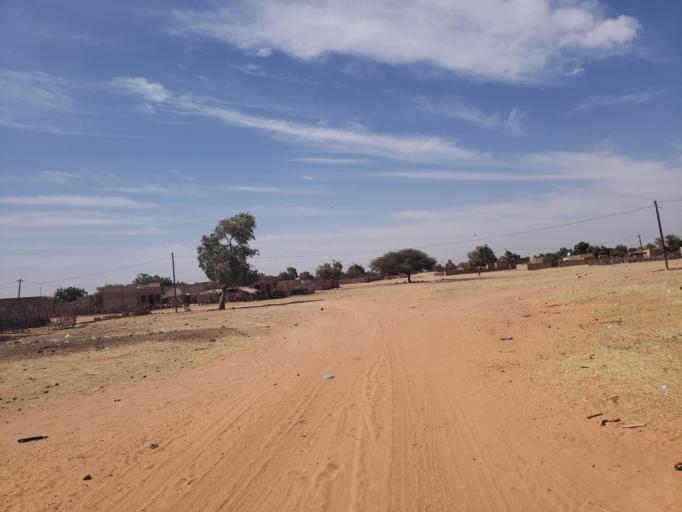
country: SN
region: Matam
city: Ranerou
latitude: 15.3032
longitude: -13.9597
